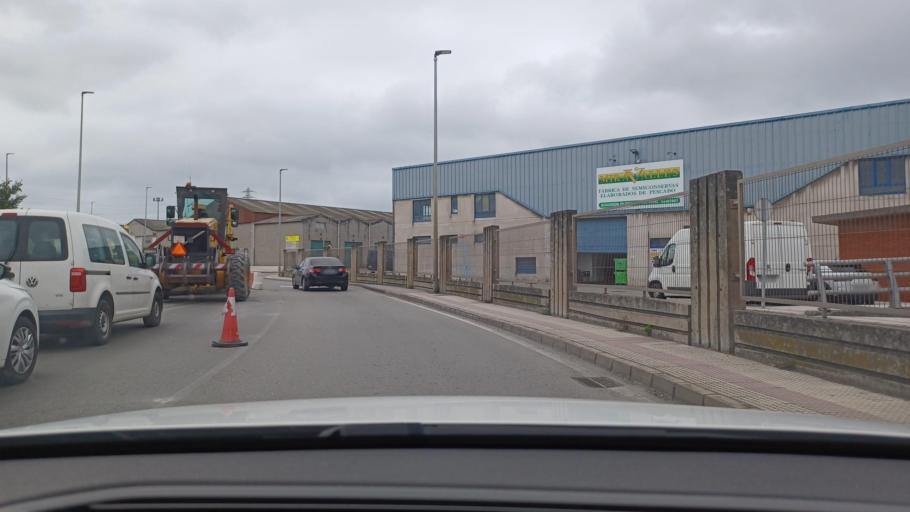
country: ES
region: Asturias
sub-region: Province of Asturias
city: Aviles
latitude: 43.5737
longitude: -5.9234
